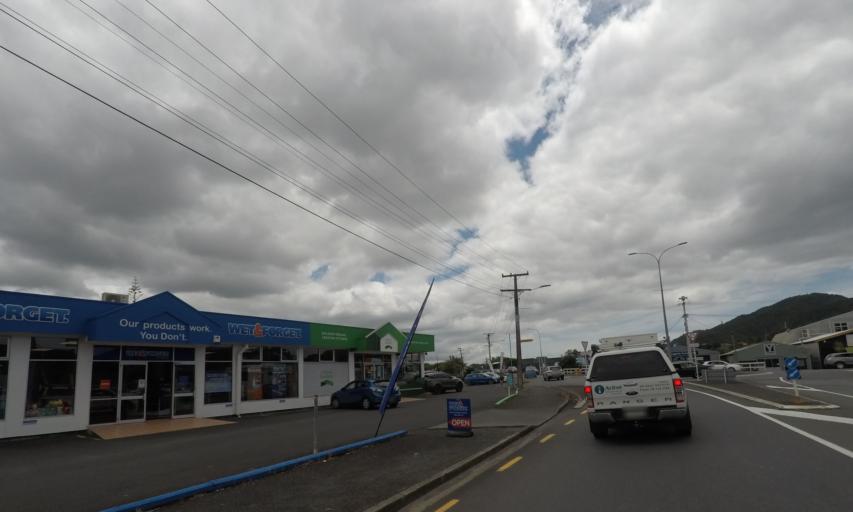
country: NZ
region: Northland
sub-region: Whangarei
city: Whangarei
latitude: -35.7301
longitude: 174.3268
